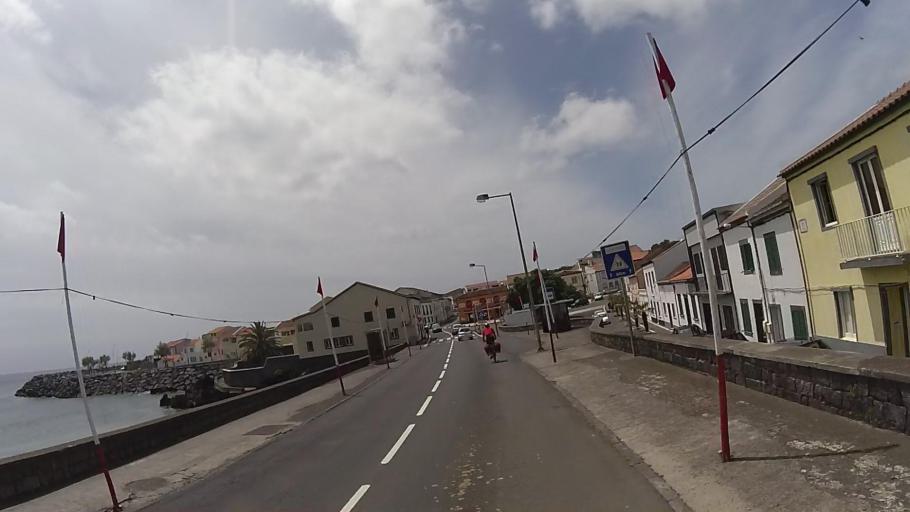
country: PT
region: Azores
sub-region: Ponta Delgada
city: Rosto de Cao
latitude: 37.7504
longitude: -25.6315
